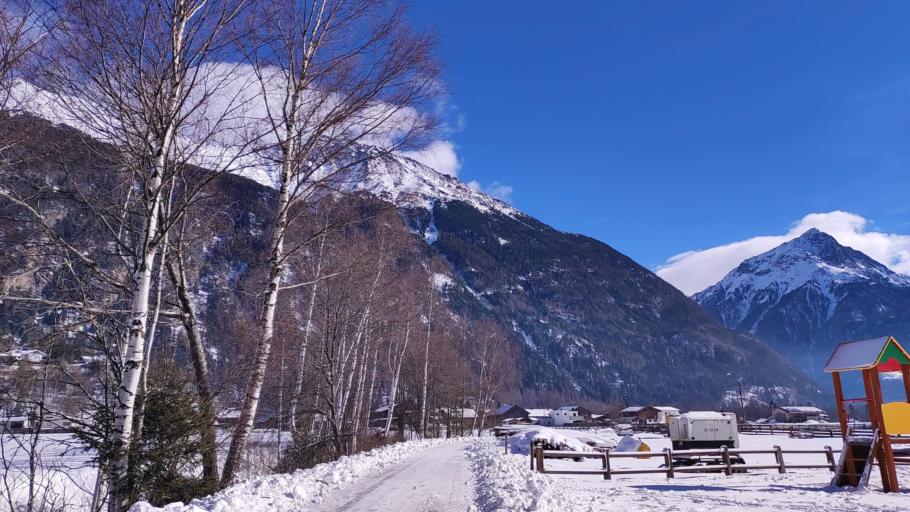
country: AT
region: Tyrol
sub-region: Politischer Bezirk Imst
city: Umhausen
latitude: 47.1008
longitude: 10.9417
